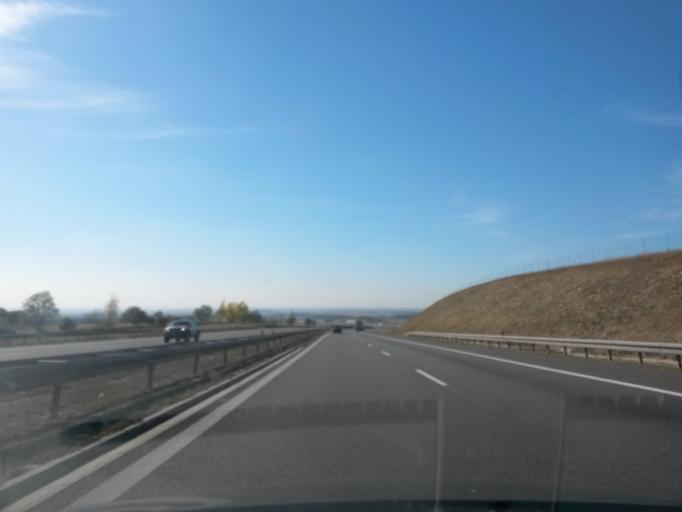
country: PL
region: Opole Voivodeship
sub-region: Powiat krapkowicki
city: Rozwadza
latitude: 50.4800
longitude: 18.1269
